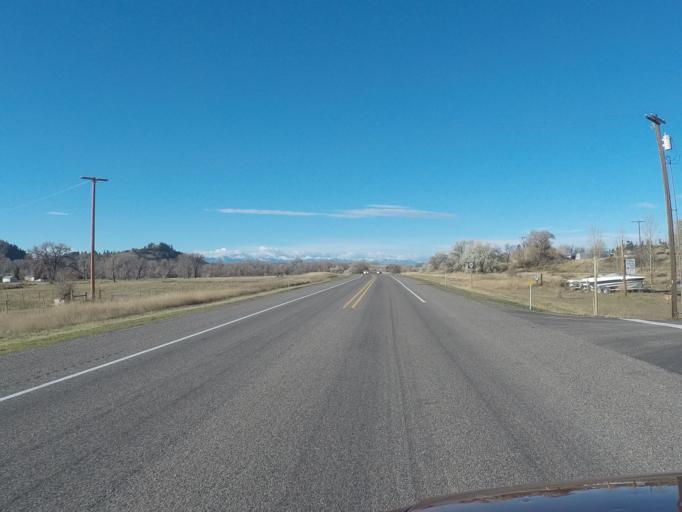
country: US
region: Montana
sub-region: Yellowstone County
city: Laurel
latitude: 45.4806
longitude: -108.9834
